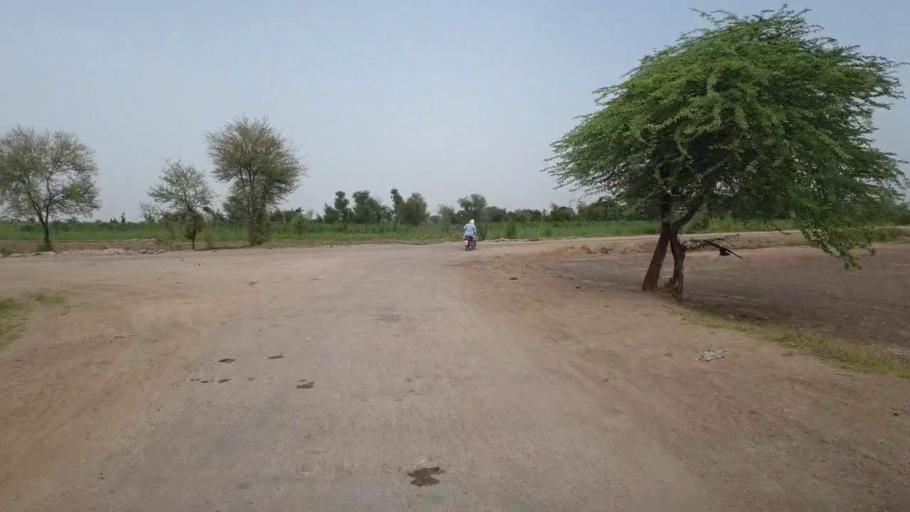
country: PK
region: Sindh
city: Daulatpur
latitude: 26.5462
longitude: 68.0891
